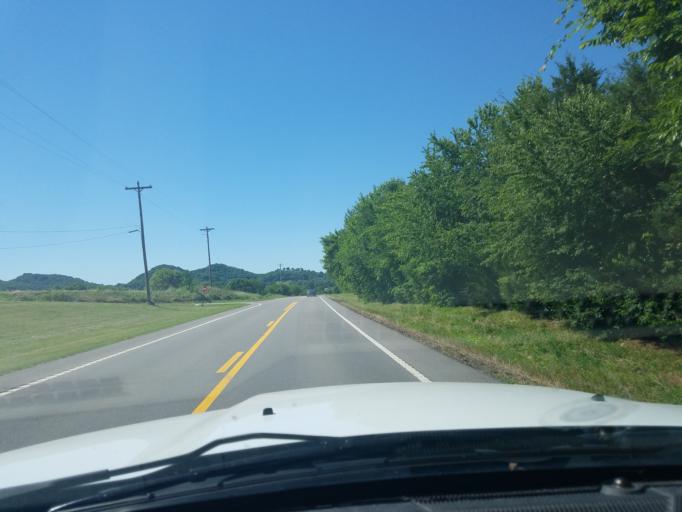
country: US
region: Tennessee
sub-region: Sumner County
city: Westmoreland
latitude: 36.4583
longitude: -86.2676
